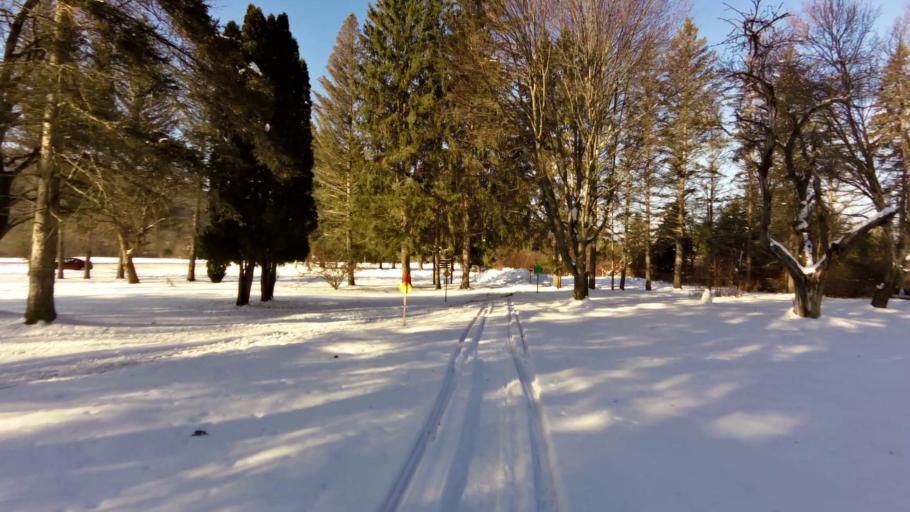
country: US
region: New York
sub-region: Cattaraugus County
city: Salamanca
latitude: 42.1064
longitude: -78.7695
